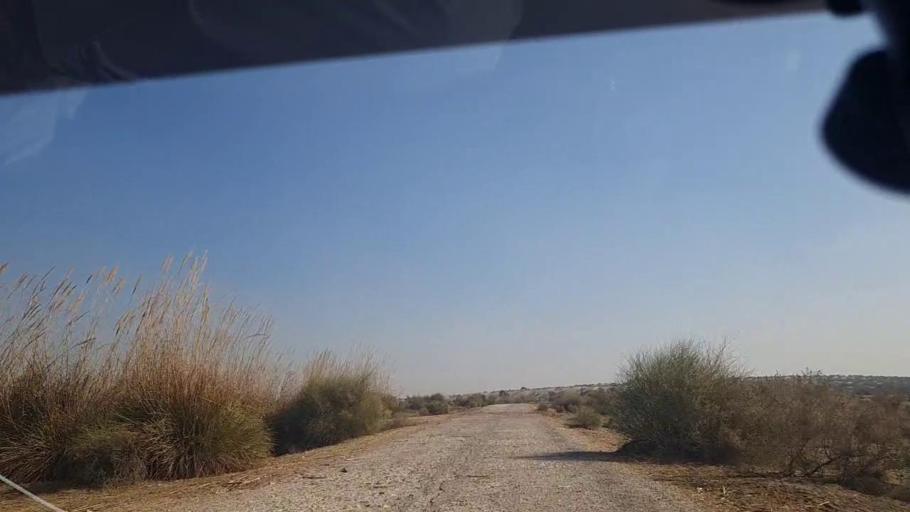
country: PK
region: Sindh
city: Khanpur
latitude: 27.5625
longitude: 69.3225
